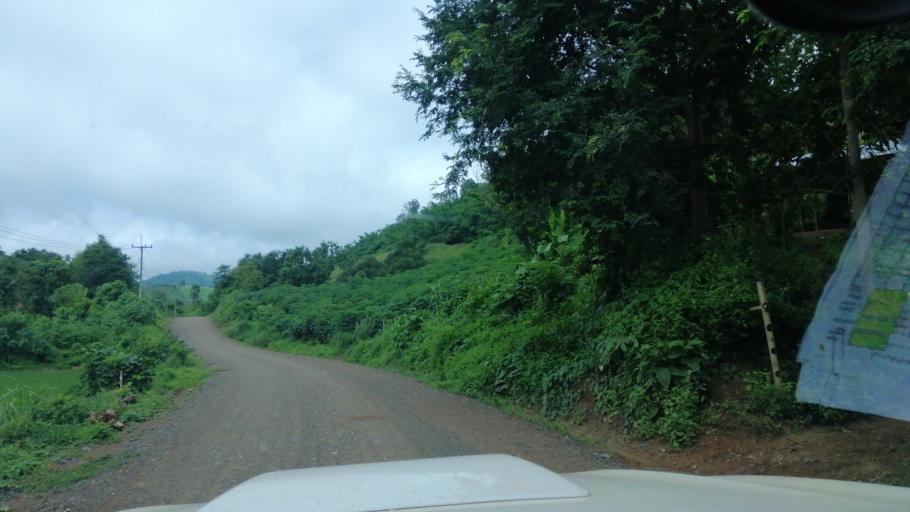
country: LA
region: Xiagnabouli
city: Muang Kenthao
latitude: 17.9176
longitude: 101.3705
